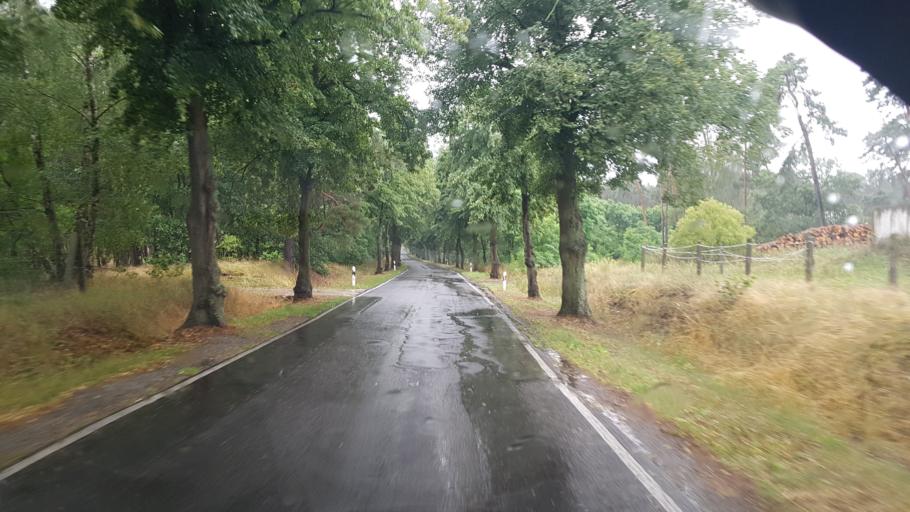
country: DE
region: Brandenburg
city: Dahme
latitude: 51.9413
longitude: 13.3956
